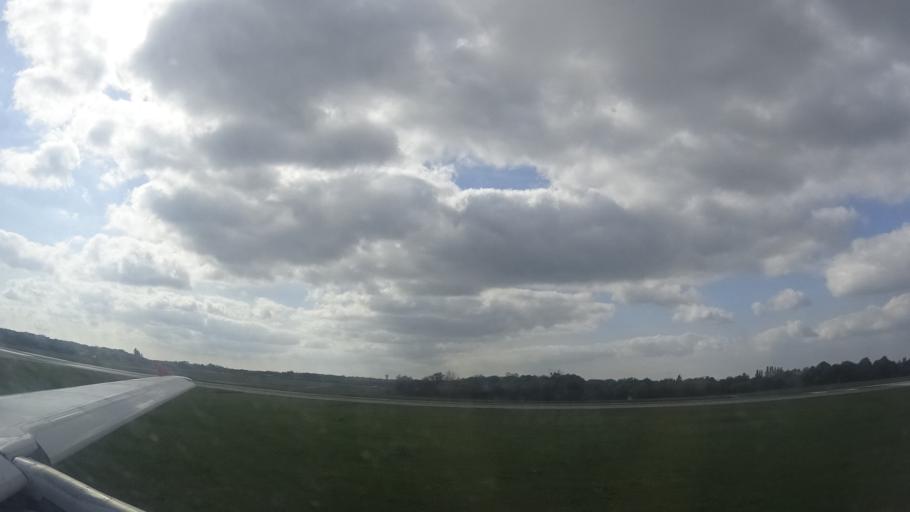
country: FR
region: Pays de la Loire
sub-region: Departement de la Loire-Atlantique
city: Bouguenais
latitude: 47.1611
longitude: -1.6019
